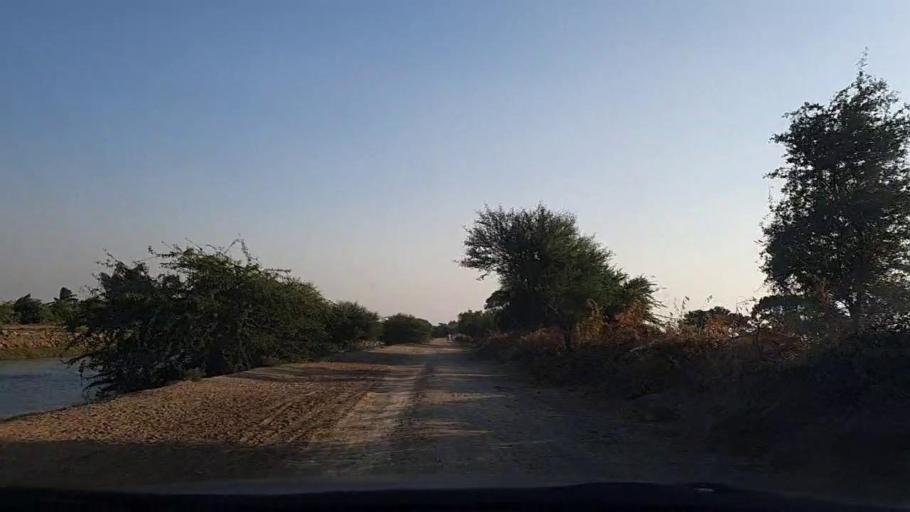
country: PK
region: Sindh
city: Mirpur Sakro
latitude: 24.5227
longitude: 67.6533
